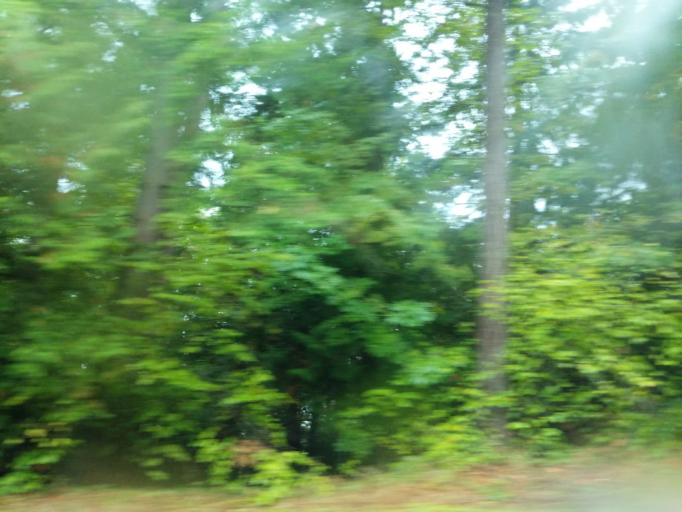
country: US
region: Washington
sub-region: King County
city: Bothell
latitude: 47.7807
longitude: -122.2073
